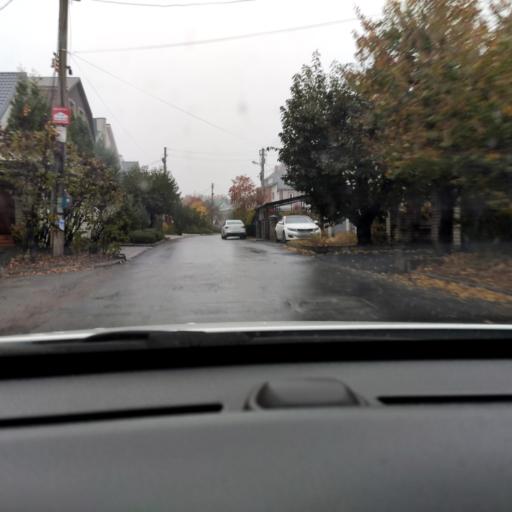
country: RU
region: Voronezj
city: Voronezh
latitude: 51.7077
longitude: 39.2004
